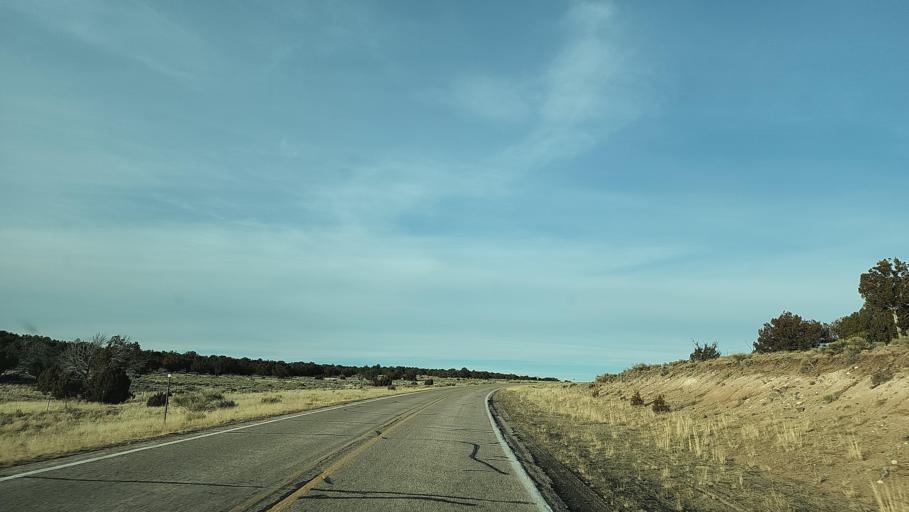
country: US
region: New Mexico
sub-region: Catron County
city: Reserve
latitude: 34.4083
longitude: -108.4363
